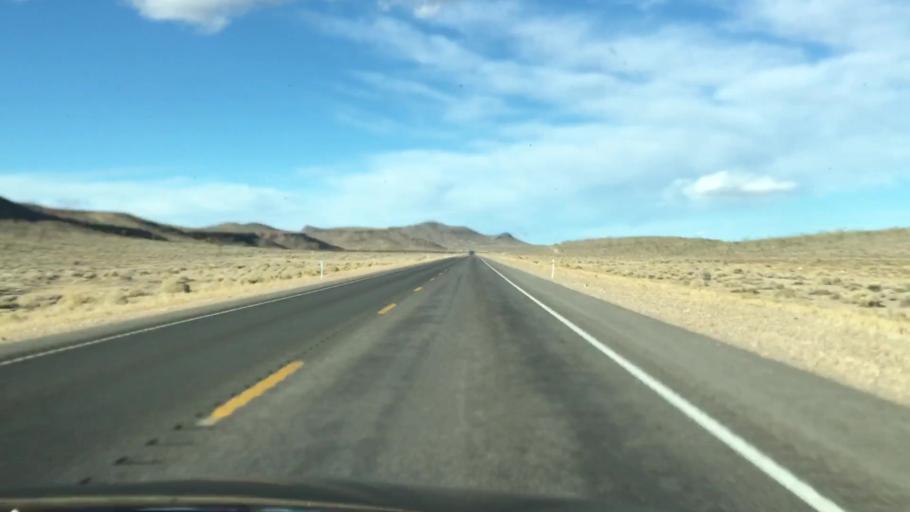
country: US
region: Nevada
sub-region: Esmeralda County
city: Goldfield
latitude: 37.6297
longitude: -117.2184
